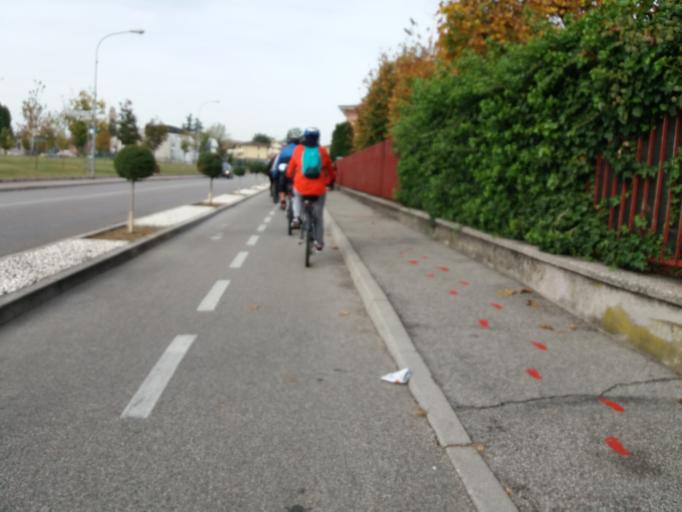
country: IT
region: Veneto
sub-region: Provincia di Verona
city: Bussolengo
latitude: 45.4716
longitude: 10.8546
